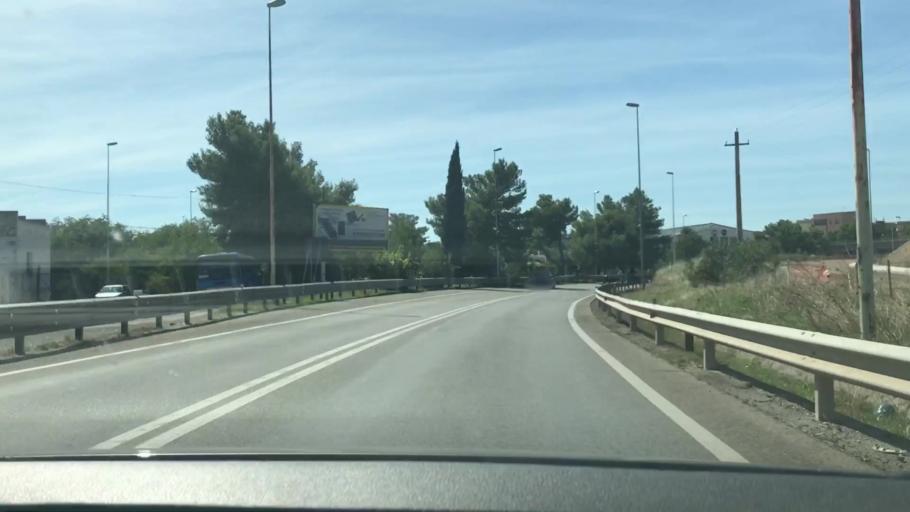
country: IT
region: Basilicate
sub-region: Provincia di Matera
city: Matera
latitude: 40.6831
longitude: 16.5901
